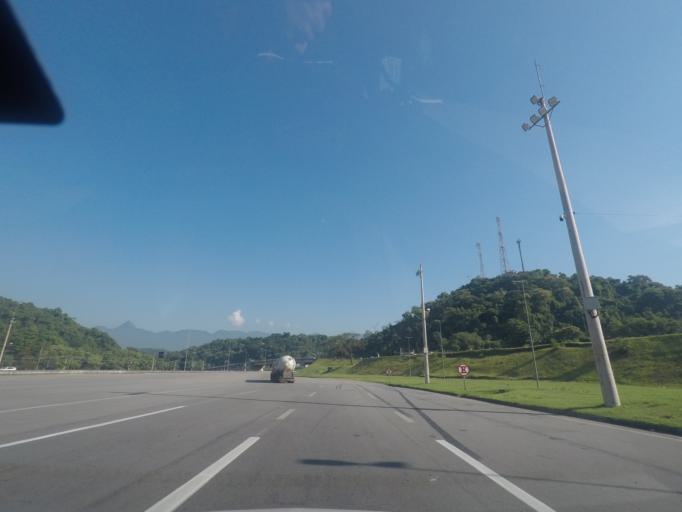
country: BR
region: Rio de Janeiro
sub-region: Petropolis
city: Petropolis
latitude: -22.6098
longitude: -43.2853
